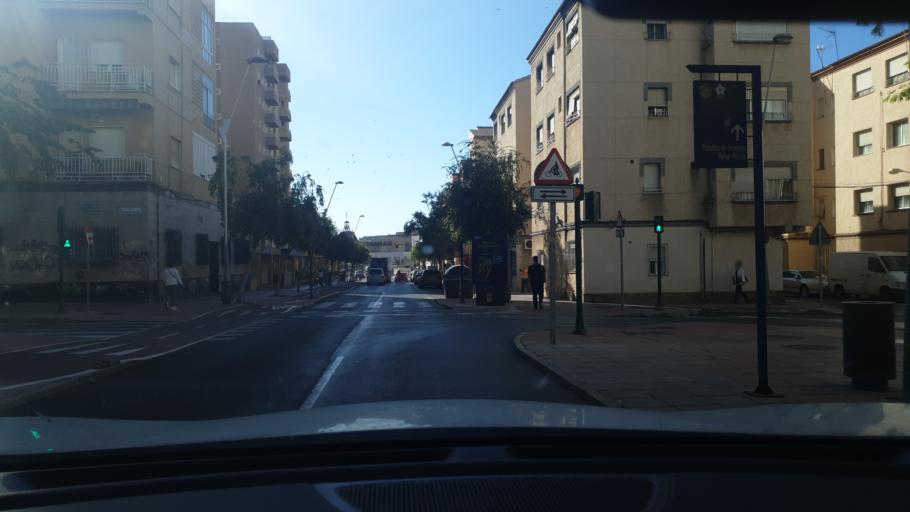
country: ES
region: Andalusia
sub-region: Provincia de Almeria
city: Almeria
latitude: 36.8403
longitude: -2.4557
